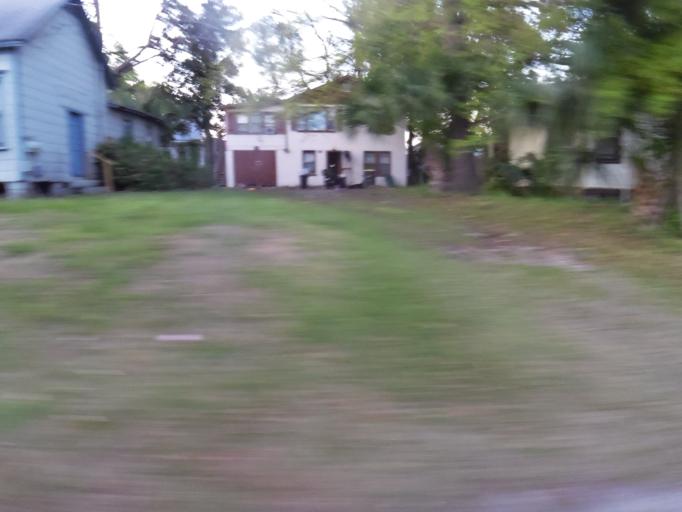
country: US
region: Florida
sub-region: Duval County
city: Jacksonville
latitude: 30.3192
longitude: -81.7029
